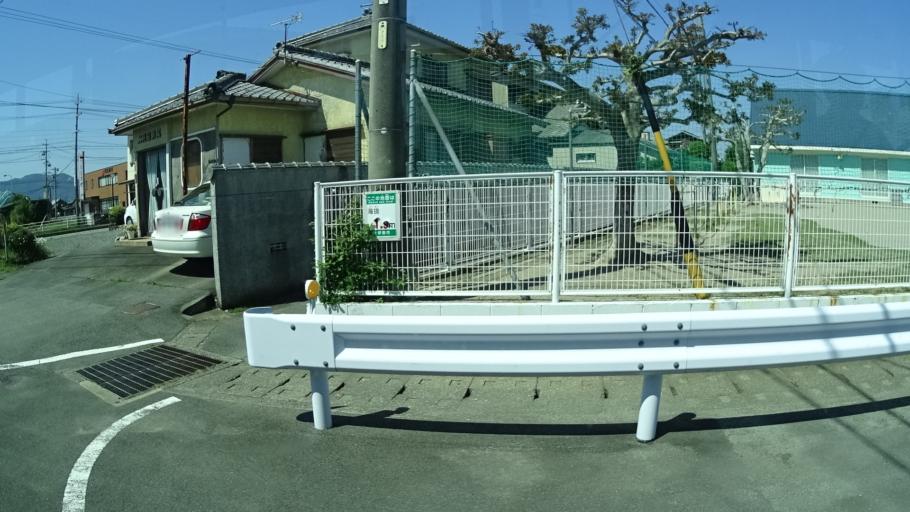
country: JP
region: Mie
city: Toba
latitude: 34.5051
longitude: 136.7759
